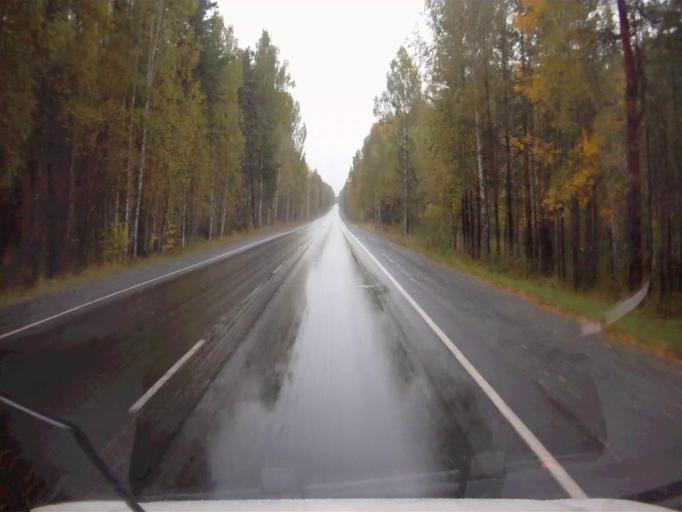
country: RU
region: Chelyabinsk
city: Tayginka
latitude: 55.5784
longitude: 60.6439
